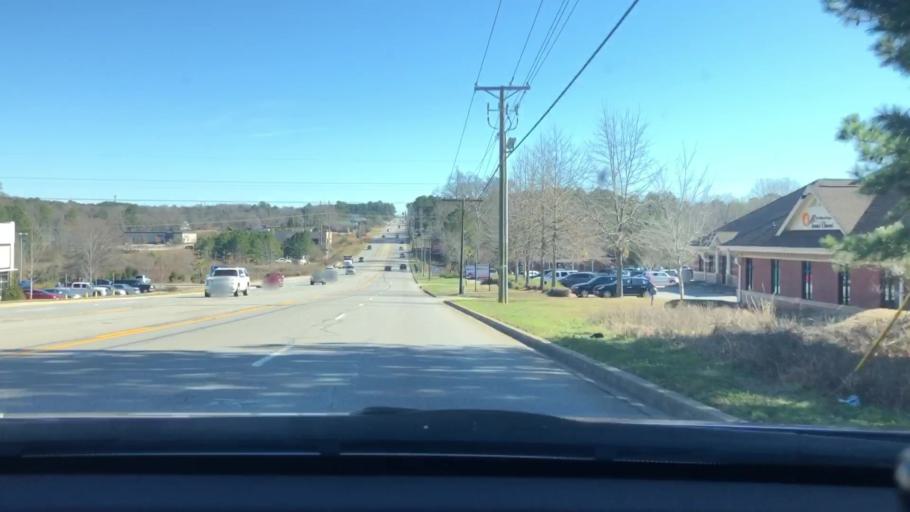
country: US
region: South Carolina
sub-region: Lexington County
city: Oak Grove
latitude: 34.0130
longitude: -81.1727
